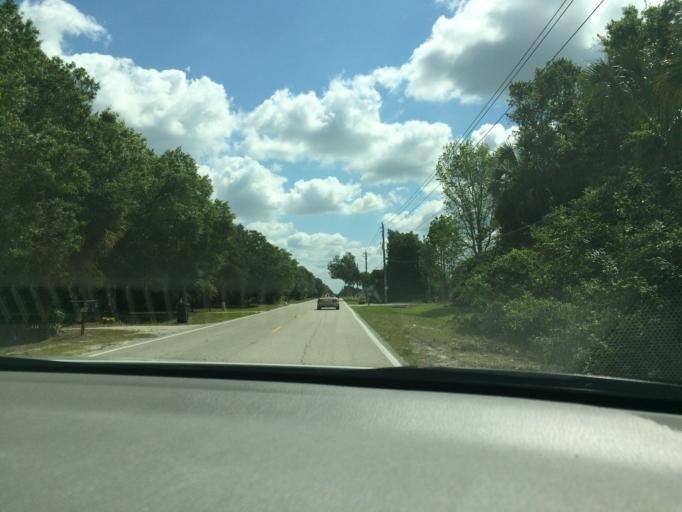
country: US
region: Florida
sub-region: Manatee County
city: Ellenton
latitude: 27.5137
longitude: -82.4231
